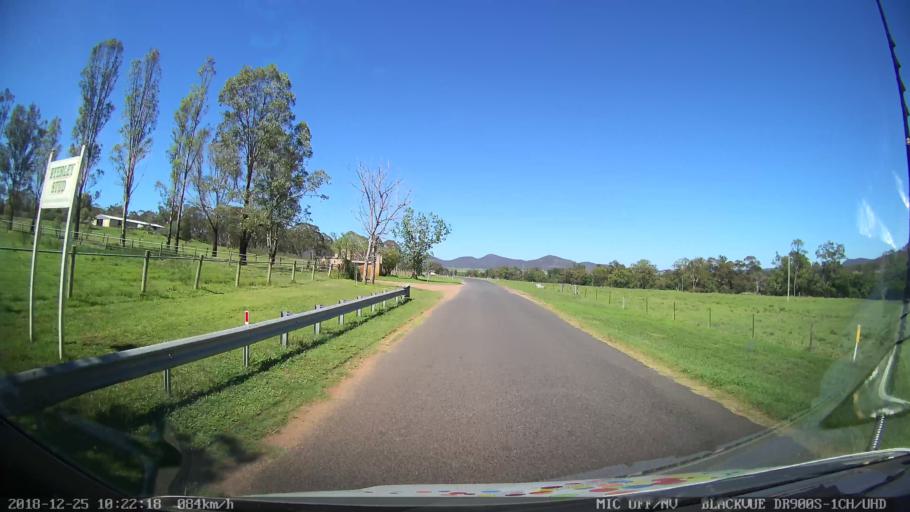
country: AU
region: New South Wales
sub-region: Muswellbrook
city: Denman
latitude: -32.3754
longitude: 150.5340
